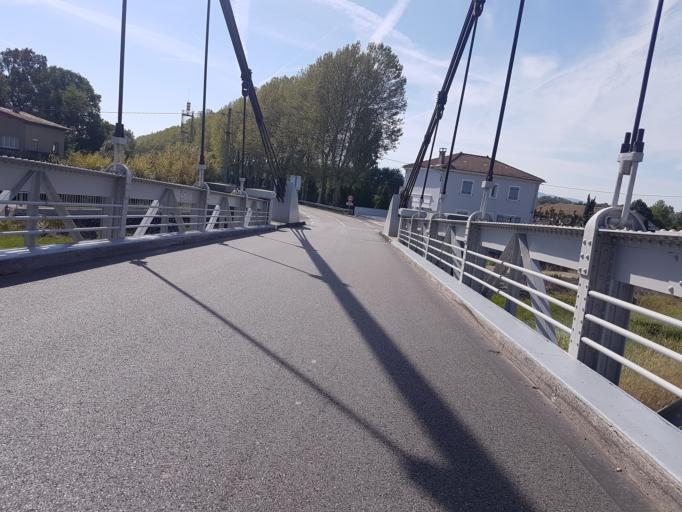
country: FR
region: Rhone-Alpes
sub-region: Departement de l'Ardeche
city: La Voulte-sur-Rhone
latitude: 44.7992
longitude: 4.7854
